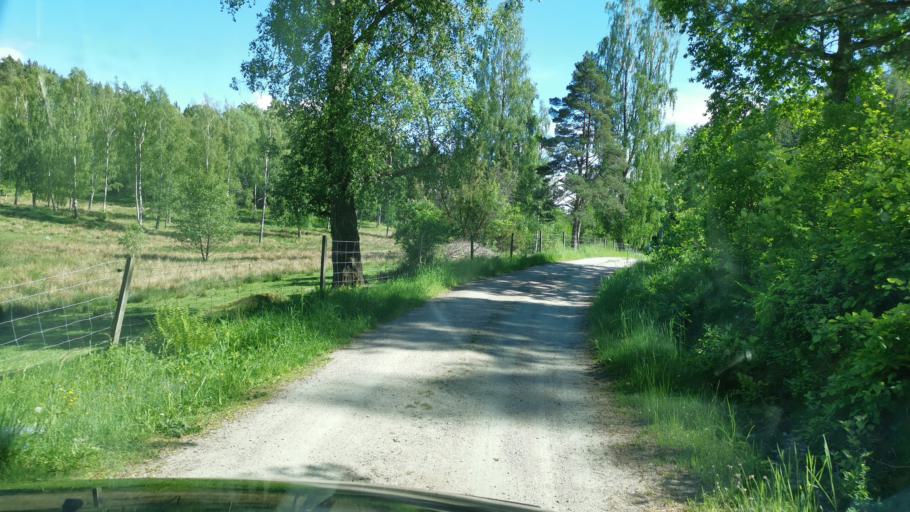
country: SE
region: Vaestra Goetaland
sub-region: Orust
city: Henan
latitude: 58.2720
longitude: 11.6396
